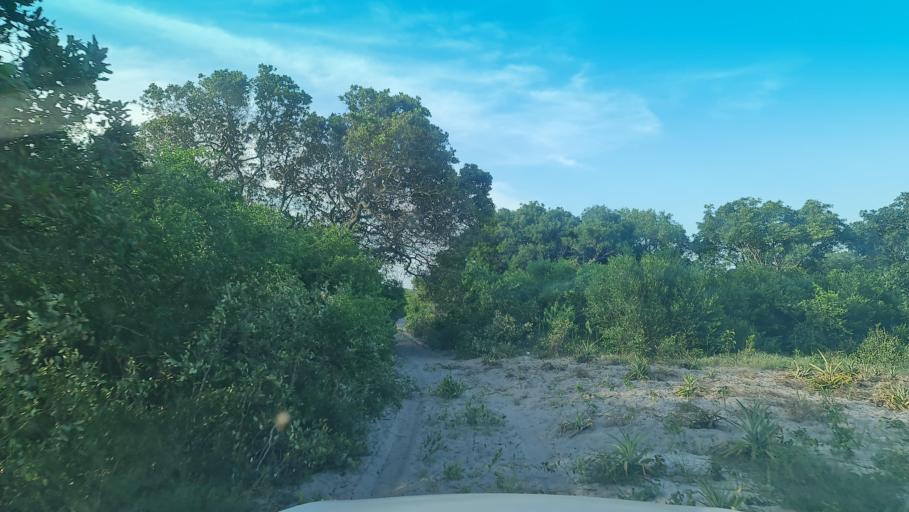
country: MZ
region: Gaza
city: Macia
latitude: -25.2325
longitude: 33.0142
